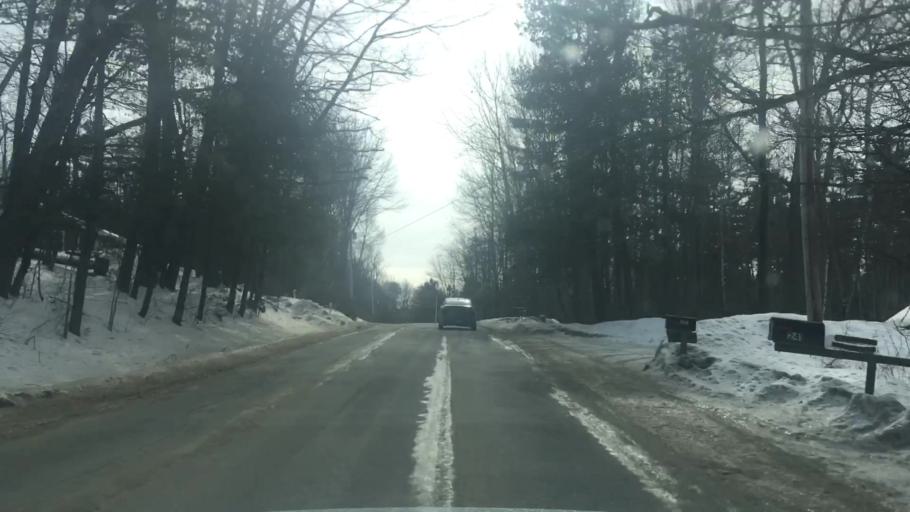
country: US
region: Maine
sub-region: Hancock County
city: Orland
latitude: 44.5885
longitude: -68.7257
